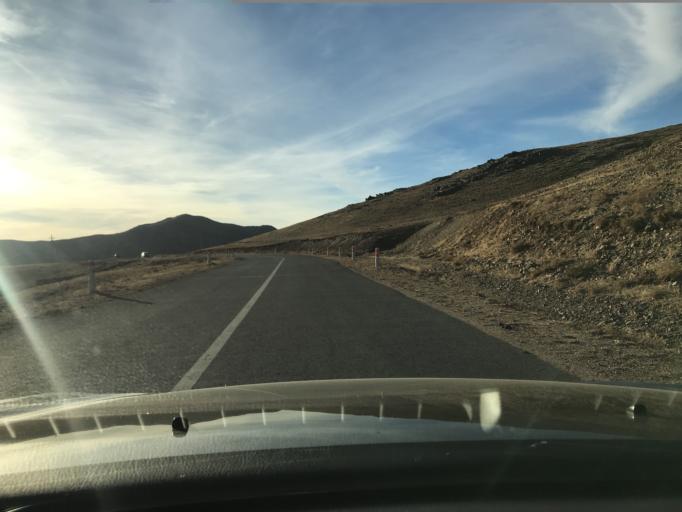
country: MN
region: Central Aimak
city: Dzuunmod
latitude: 47.8254
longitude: 107.3431
